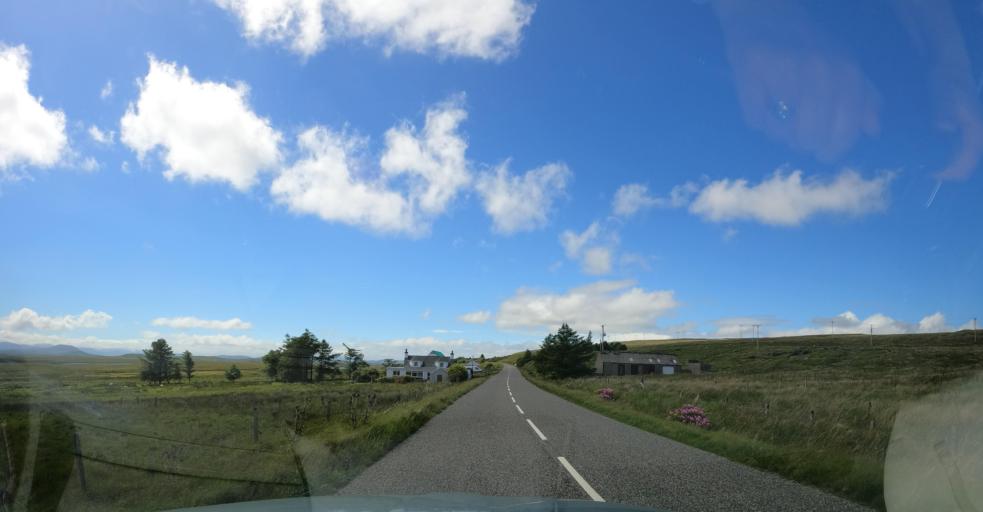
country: GB
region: Scotland
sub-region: Eilean Siar
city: Stornoway
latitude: 58.1649
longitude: -6.5492
